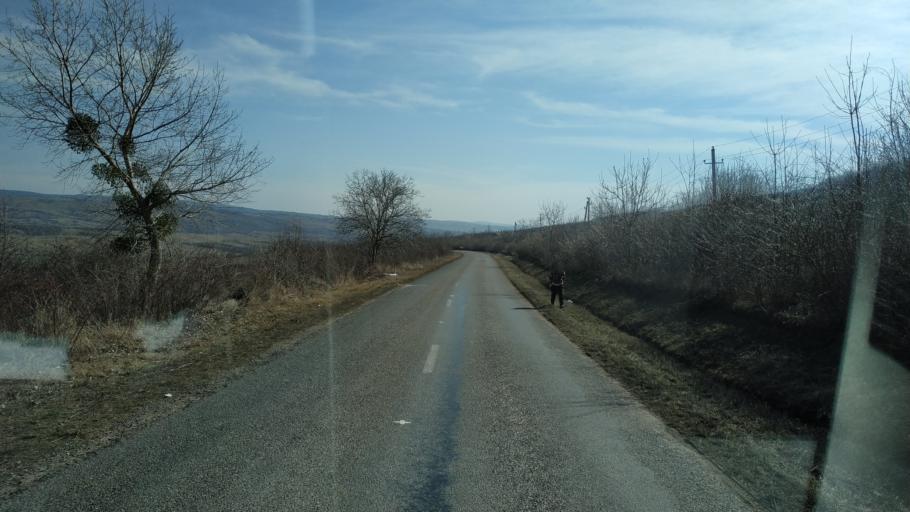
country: MD
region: Nisporeni
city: Nisporeni
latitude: 47.1811
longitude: 28.0788
